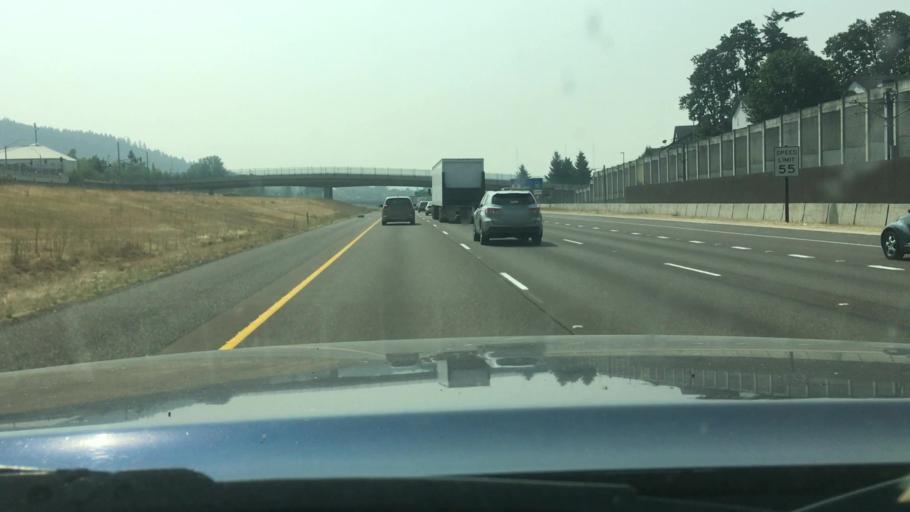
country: US
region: Oregon
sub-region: Clackamas County
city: Clackamas
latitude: 45.4405
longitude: -122.5689
